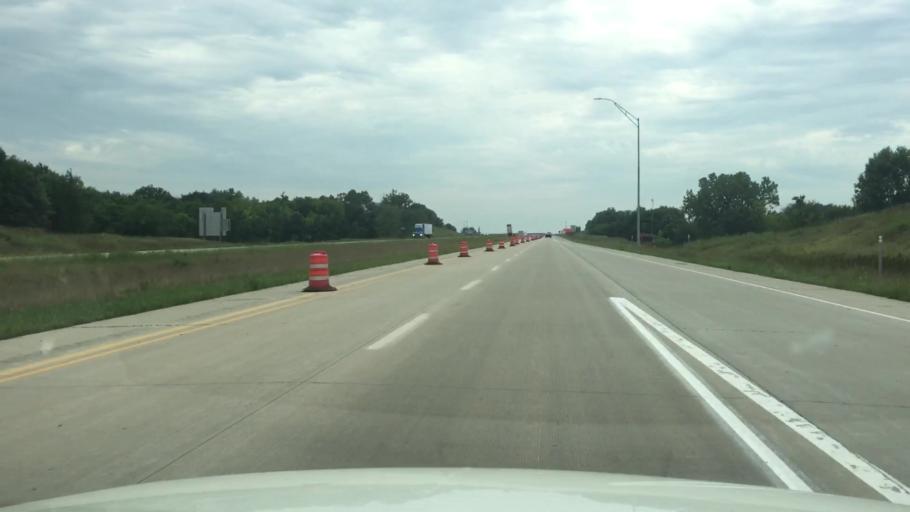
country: US
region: Iowa
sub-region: Decatur County
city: Leon
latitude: 40.7339
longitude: -93.8434
